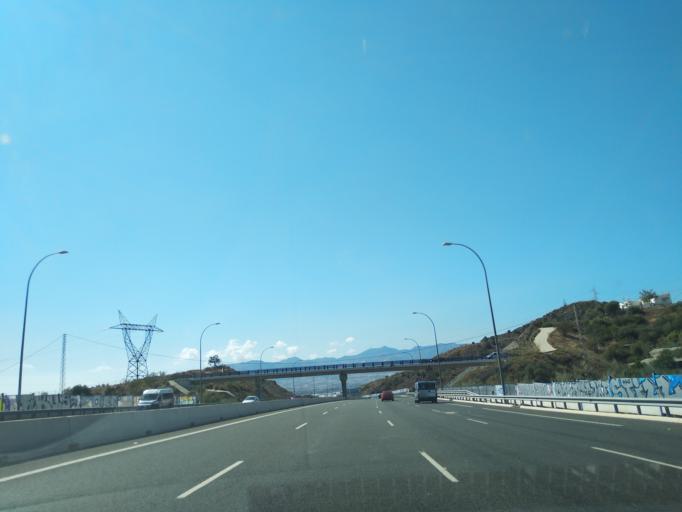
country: ES
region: Andalusia
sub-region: Provincia de Malaga
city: Malaga
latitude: 36.7391
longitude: -4.5040
